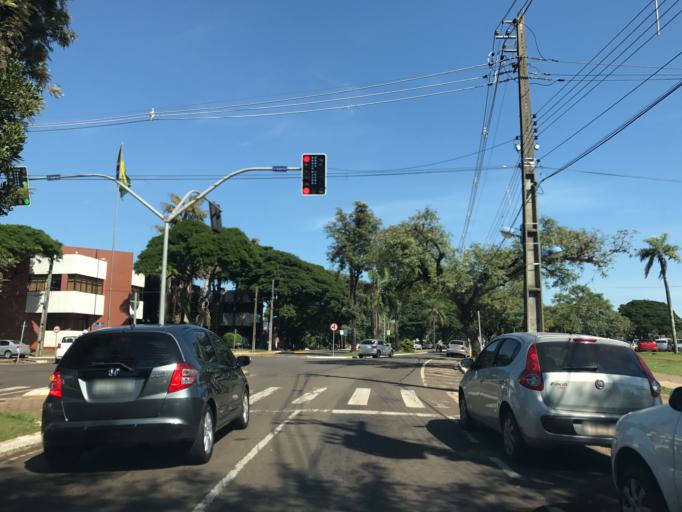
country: BR
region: Parana
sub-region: Maringa
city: Maringa
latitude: -23.4273
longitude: -51.9373
